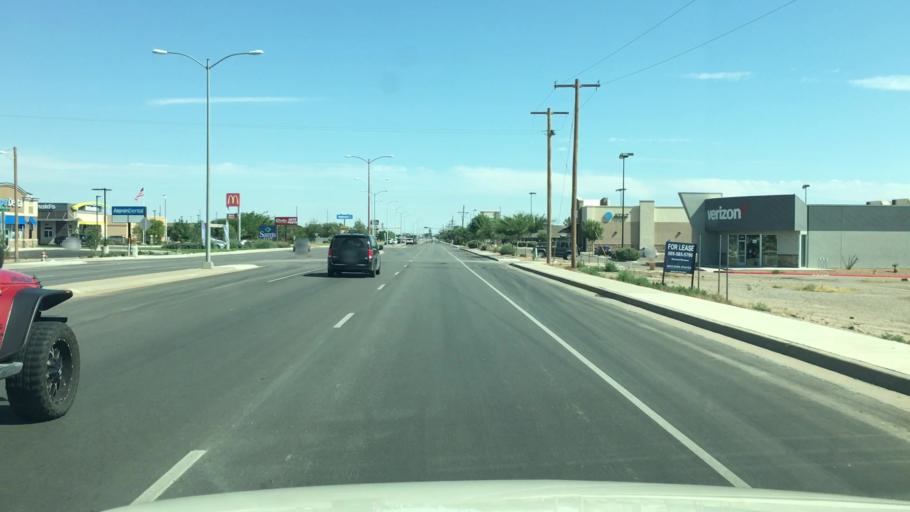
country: US
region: New Mexico
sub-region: Chaves County
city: Roswell
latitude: 33.4456
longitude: -104.5232
